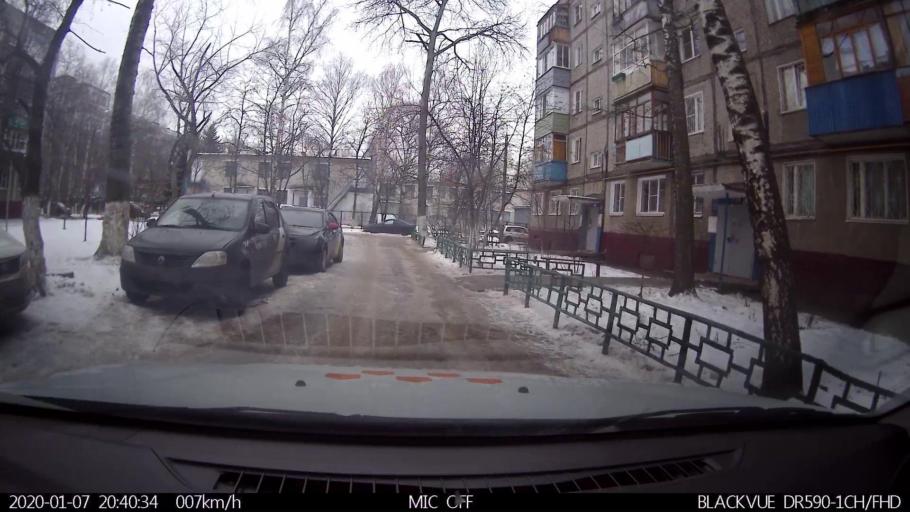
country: RU
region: Nizjnij Novgorod
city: Gorbatovka
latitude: 56.2595
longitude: 43.8782
